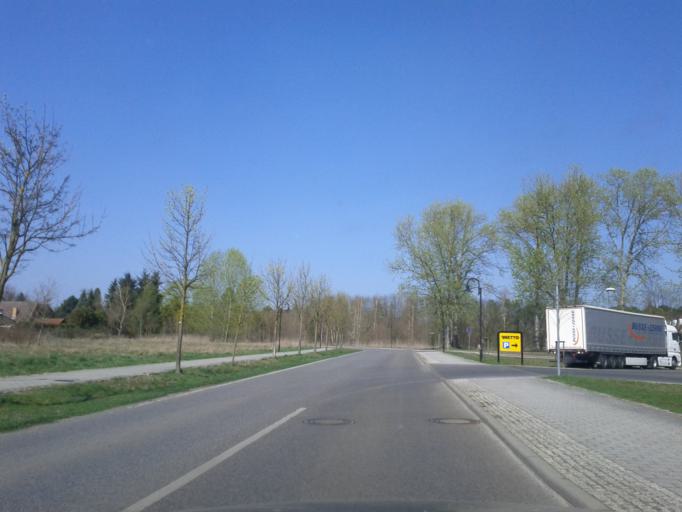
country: DE
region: Brandenburg
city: Woltersdorf
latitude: 52.4546
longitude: 13.7376
